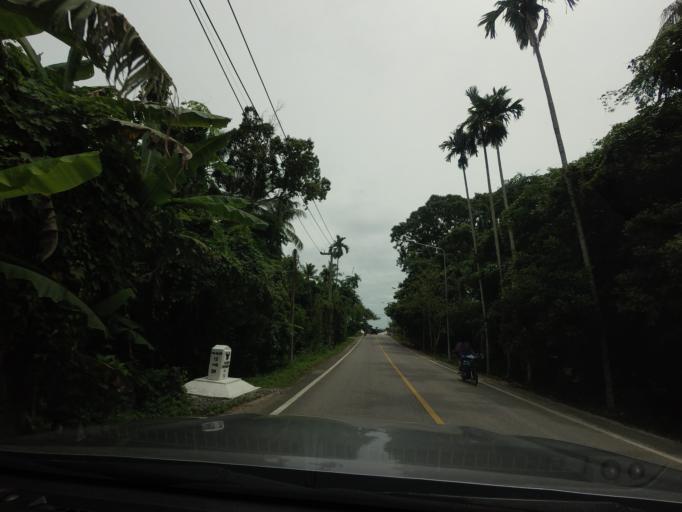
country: TH
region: Pattani
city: Kapho
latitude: 6.5894
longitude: 101.5327
